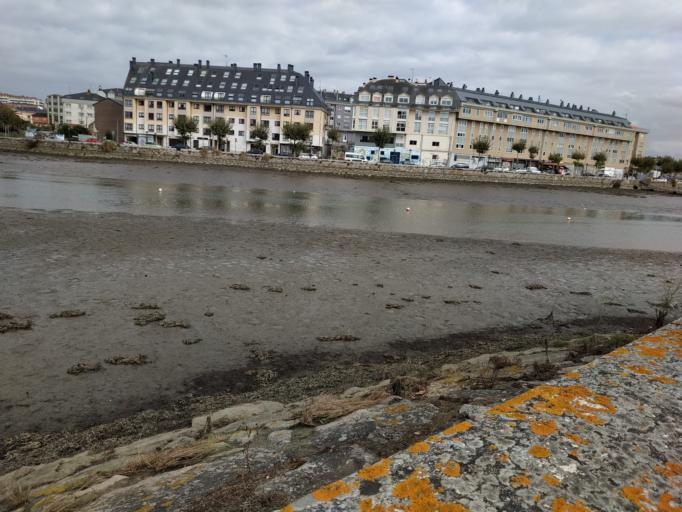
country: ES
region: Galicia
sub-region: Provincia da Coruna
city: Cambre
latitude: 43.3140
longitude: -8.3603
